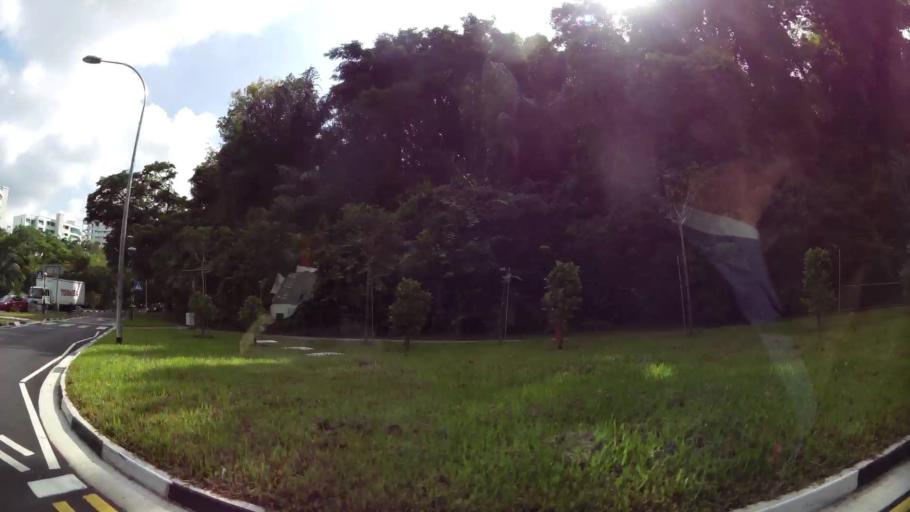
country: SG
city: Singapore
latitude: 1.2701
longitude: 103.8254
